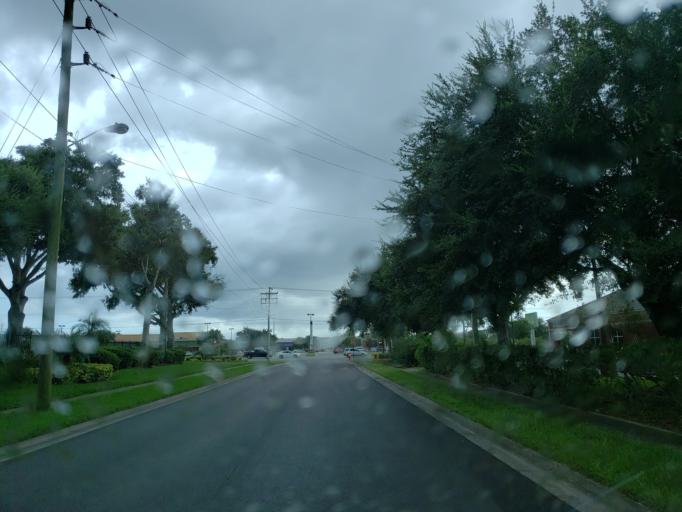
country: US
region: Florida
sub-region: Hillsborough County
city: Brandon
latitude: 27.9243
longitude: -82.3208
